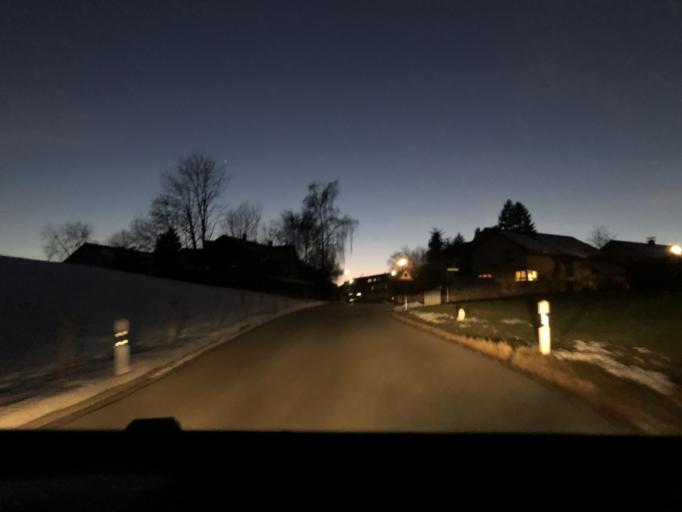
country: DE
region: Bavaria
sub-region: Swabia
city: Waltenhofen
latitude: 47.6699
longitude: 10.3131
